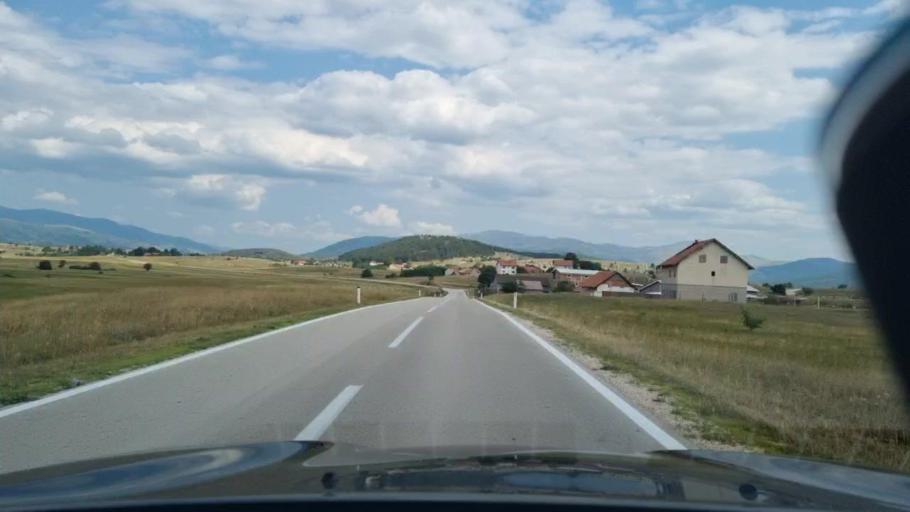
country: BA
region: Federation of Bosnia and Herzegovina
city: Bosansko Grahovo
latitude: 44.1605
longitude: 16.3886
